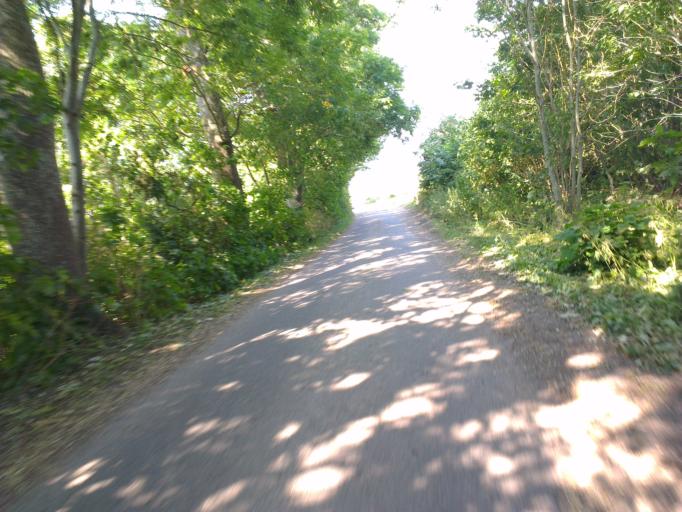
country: DK
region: Capital Region
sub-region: Frederikssund Kommune
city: Skibby
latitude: 55.7957
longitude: 11.9171
